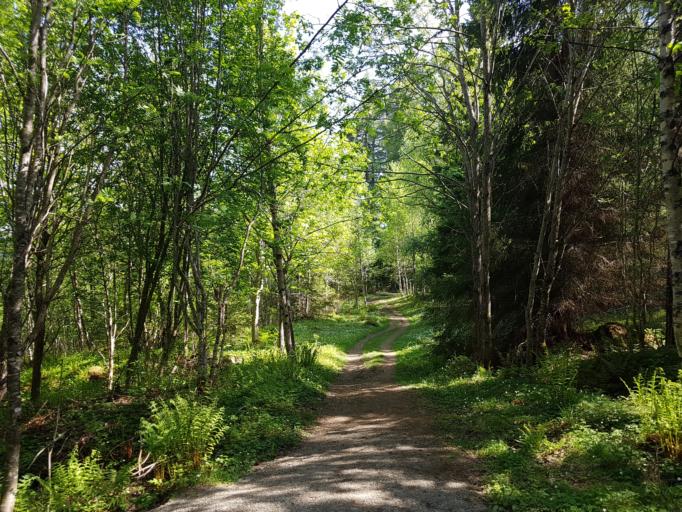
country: NO
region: Sor-Trondelag
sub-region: Trondheim
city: Trondheim
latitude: 63.4292
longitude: 10.3410
